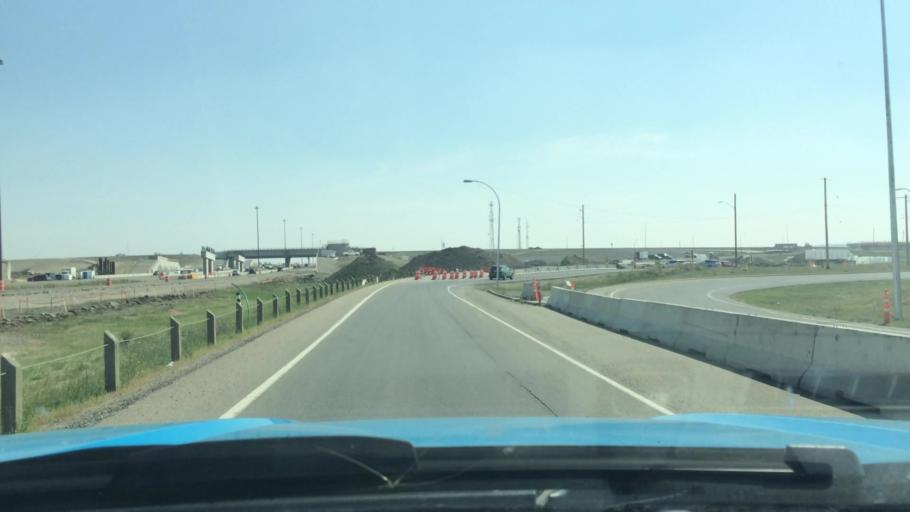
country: CA
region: Alberta
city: Calgary
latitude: 50.8971
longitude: -114.0579
